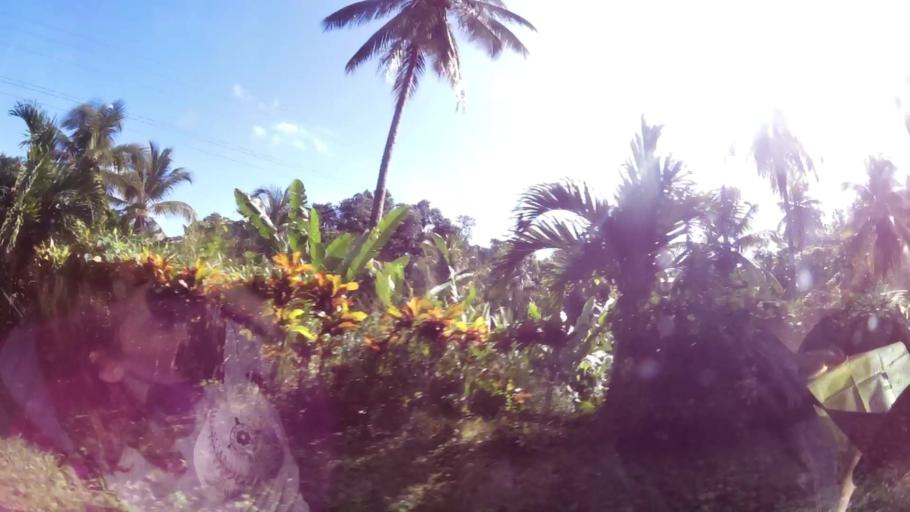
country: DM
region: Saint Andrew
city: Marigot
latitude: 15.5171
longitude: -61.2651
